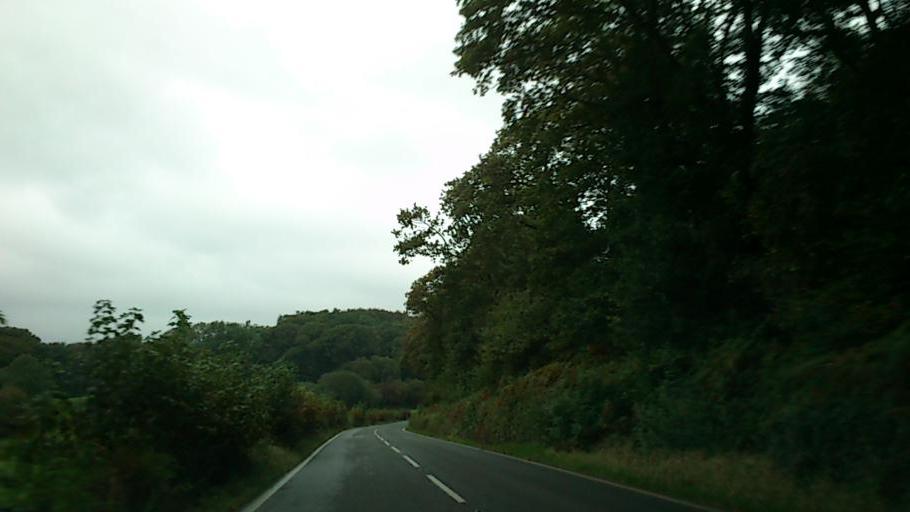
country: GB
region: Wales
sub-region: County of Ceredigion
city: Bow Street
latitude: 52.5153
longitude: -3.9736
